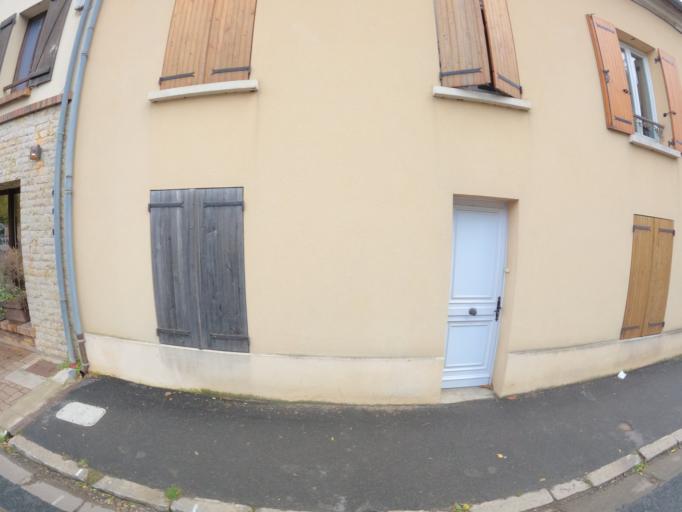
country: FR
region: Ile-de-France
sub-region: Departement de Seine-et-Marne
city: Saint-Germain-sur-Morin
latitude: 48.8823
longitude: 2.8512
